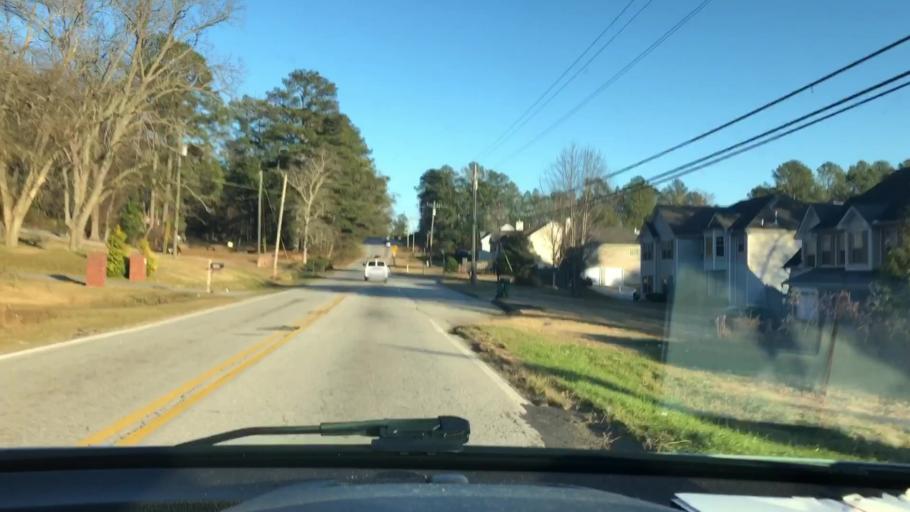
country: US
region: Georgia
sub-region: DeKalb County
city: Lithonia
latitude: 33.7346
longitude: -84.0786
